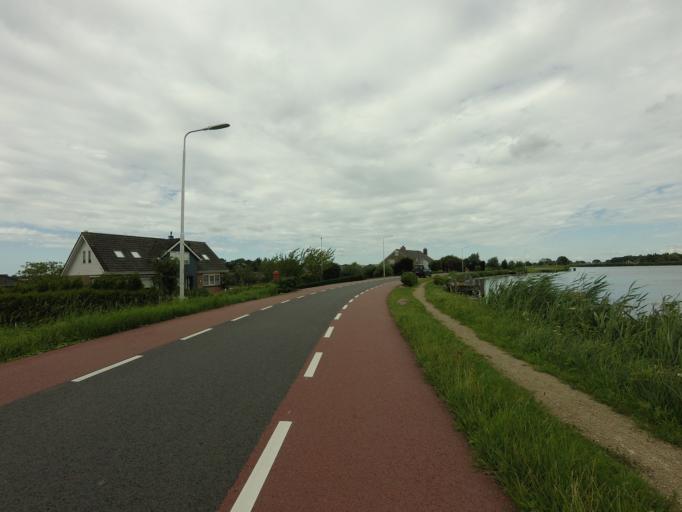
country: NL
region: North Holland
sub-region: Gemeente Uithoorn
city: Uithoorn
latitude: 52.2459
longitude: 4.8550
